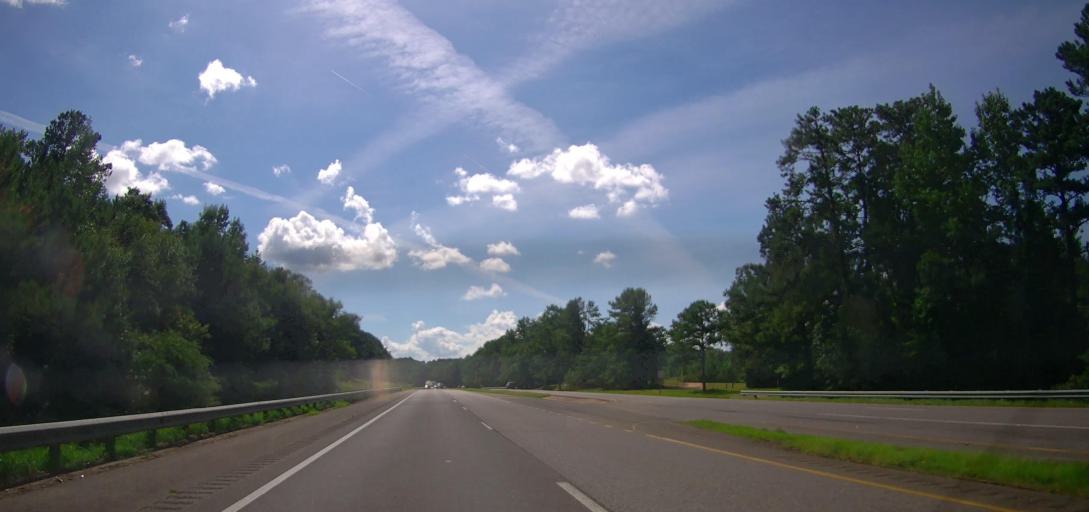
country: US
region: Alabama
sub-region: Pickens County
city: Gordo
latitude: 33.2838
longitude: -87.8331
